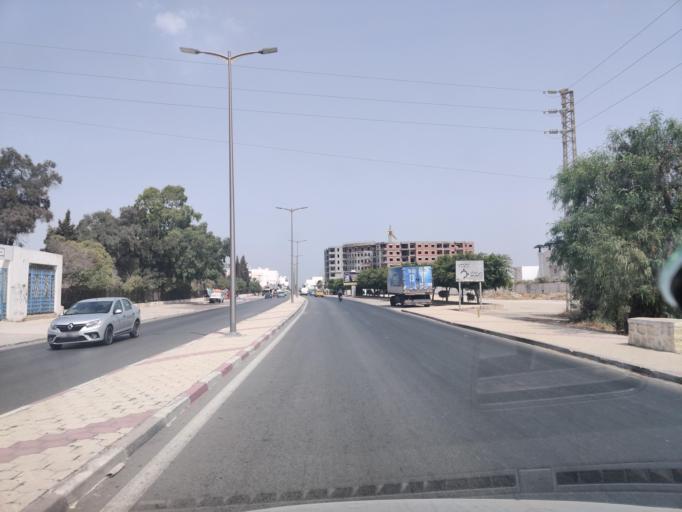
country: TN
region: Nabul
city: Bu `Urqub
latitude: 36.5922
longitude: 10.5034
